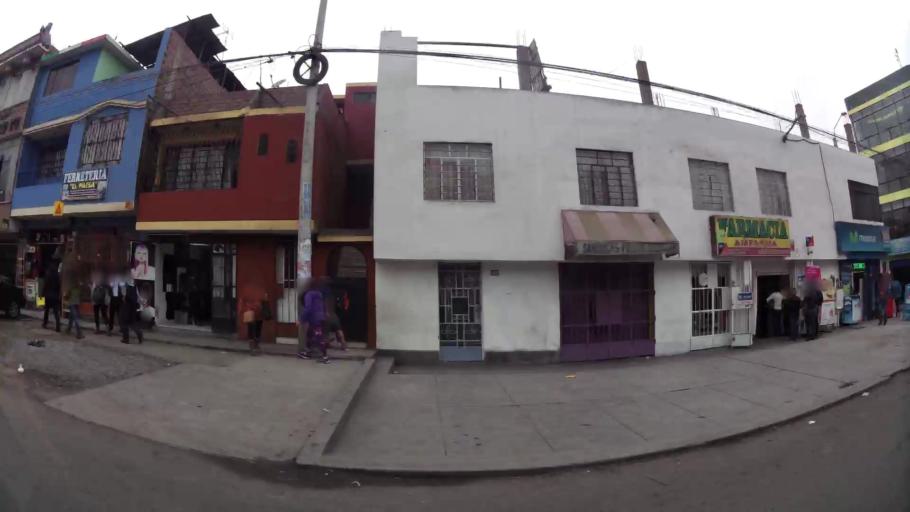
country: PE
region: Lima
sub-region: Lima
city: Independencia
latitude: -11.9482
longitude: -76.9842
